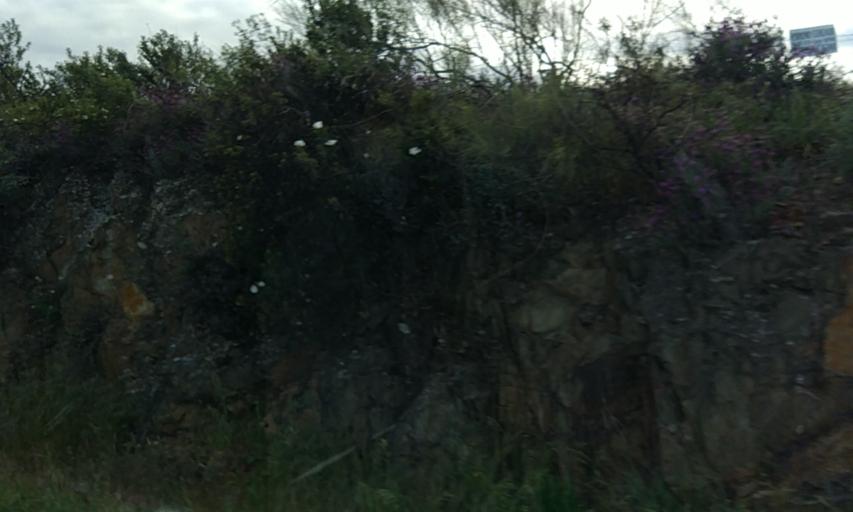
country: ES
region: Extremadura
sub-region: Provincia de Caceres
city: Coria
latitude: 39.9433
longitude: -6.5075
